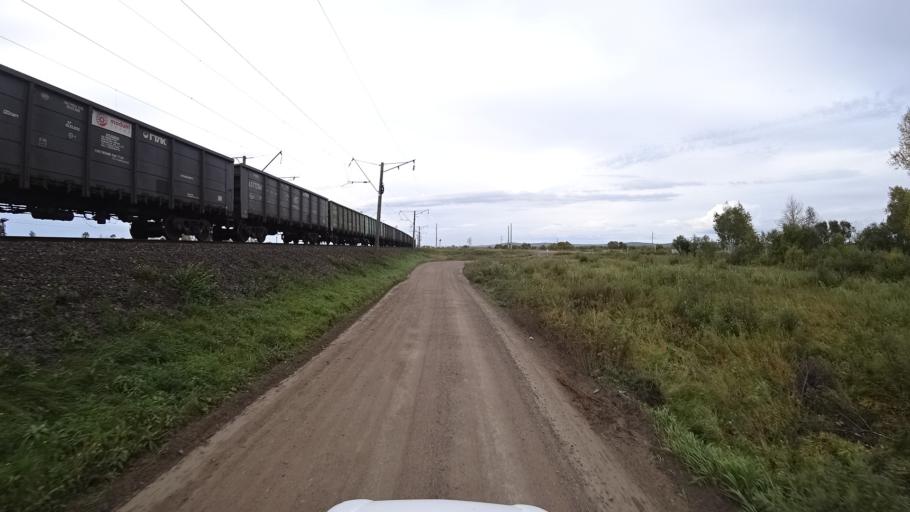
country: RU
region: Amur
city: Arkhara
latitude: 49.3697
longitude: 130.1409
